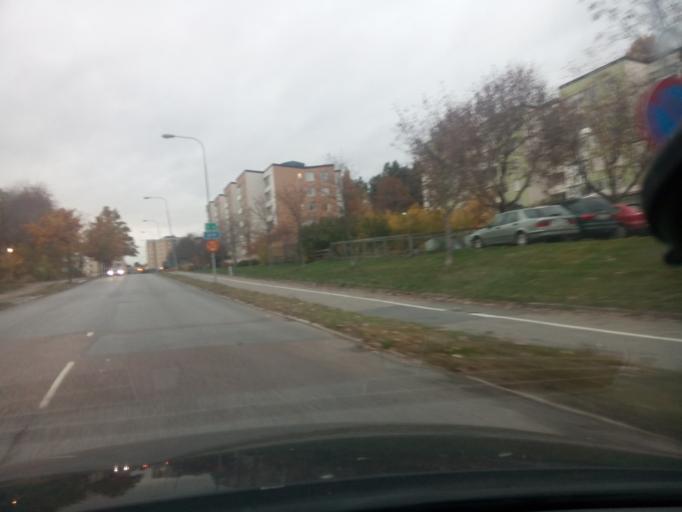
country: SE
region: Soedermanland
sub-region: Nykopings Kommun
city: Nykoping
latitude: 58.7548
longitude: 17.0417
